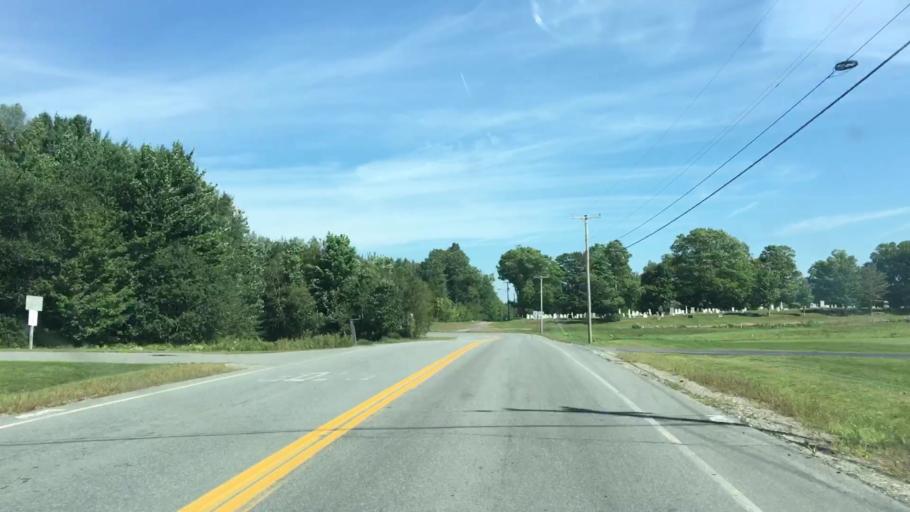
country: US
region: Maine
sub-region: Penobscot County
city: Bradford
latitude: 45.1668
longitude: -68.8434
